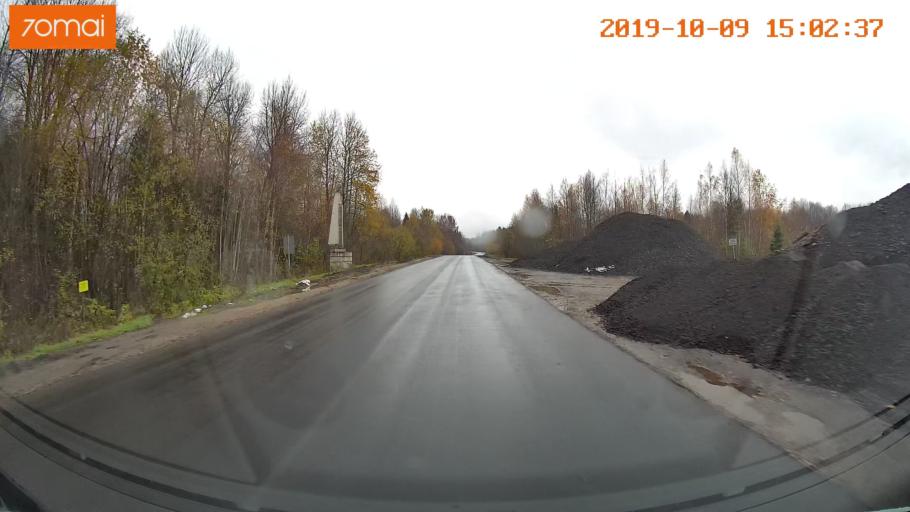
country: RU
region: Kostroma
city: Chistyye Bory
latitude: 58.2825
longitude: 41.6782
